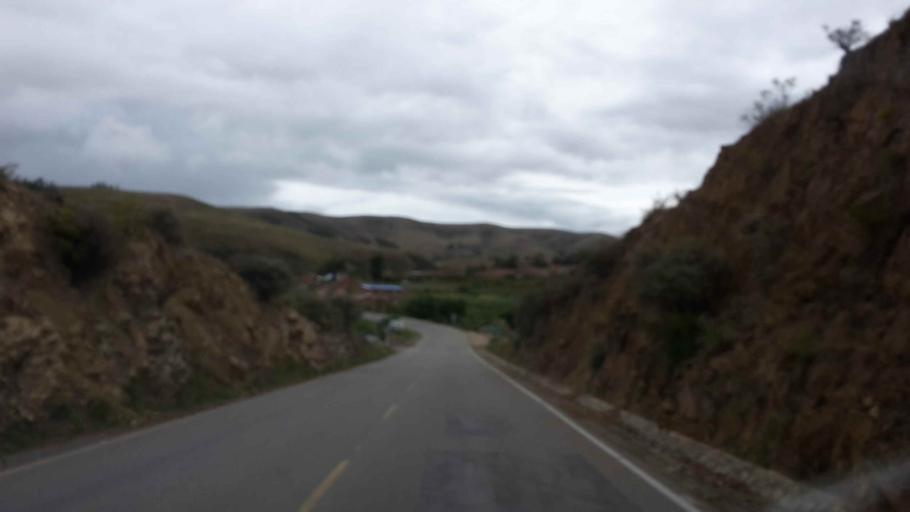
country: BO
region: Cochabamba
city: Arani
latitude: -17.4805
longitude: -65.7674
